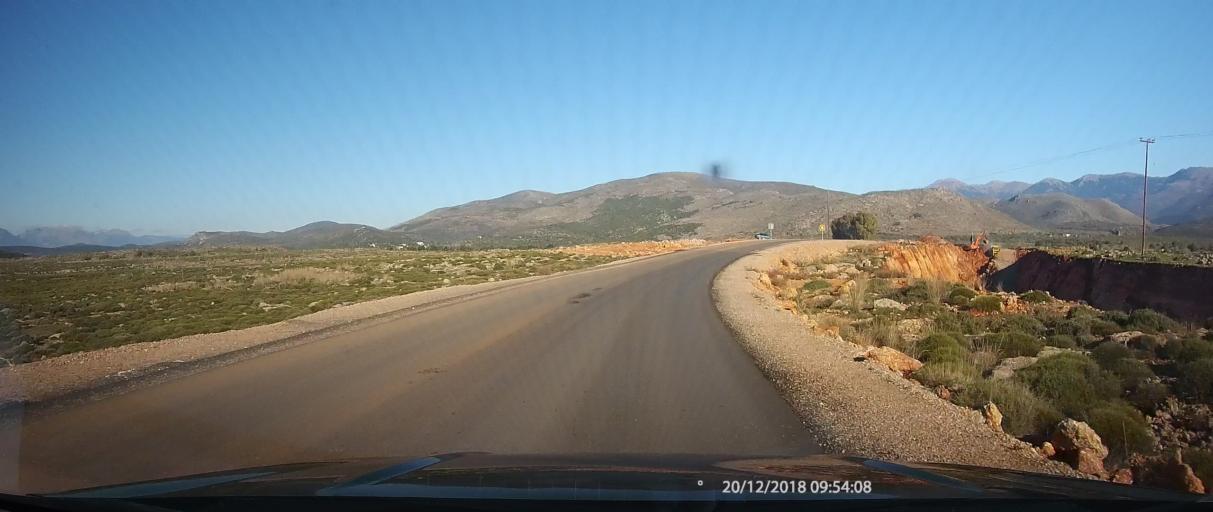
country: GR
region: Peloponnese
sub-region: Nomos Lakonias
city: Yerakion
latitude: 37.0134
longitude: 22.6361
